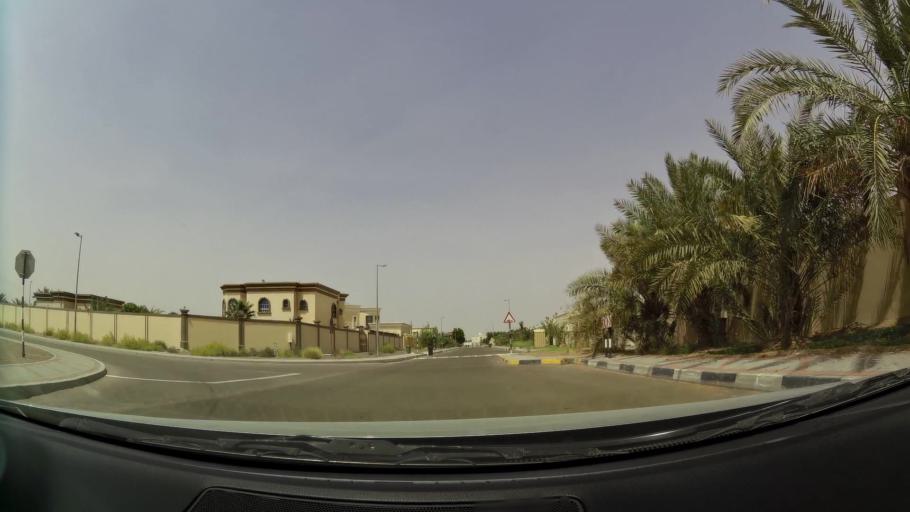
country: AE
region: Abu Dhabi
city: Al Ain
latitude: 24.1455
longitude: 55.6360
